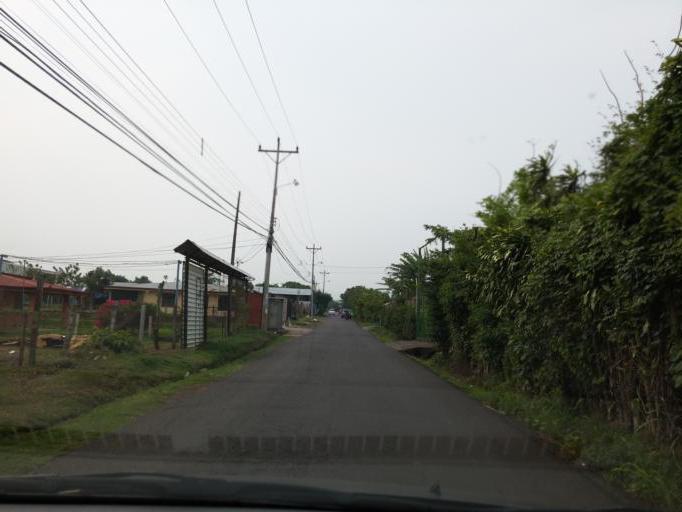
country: CR
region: Alajuela
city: Alajuela
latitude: 9.9825
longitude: -84.2253
